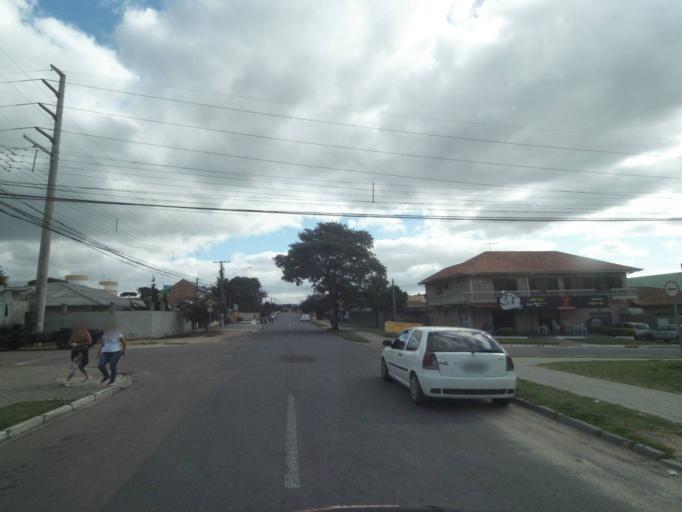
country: BR
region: Parana
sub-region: Sao Jose Dos Pinhais
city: Sao Jose dos Pinhais
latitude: -25.5536
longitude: -49.2526
